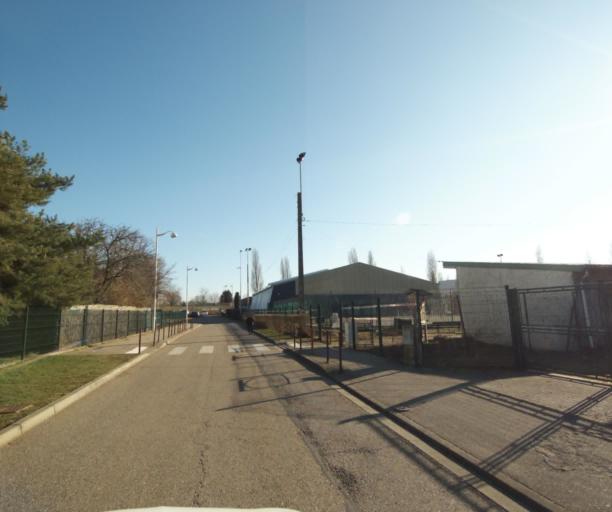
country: FR
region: Lorraine
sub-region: Departement de Meurthe-et-Moselle
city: Essey-les-Nancy
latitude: 48.6990
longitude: 6.2206
